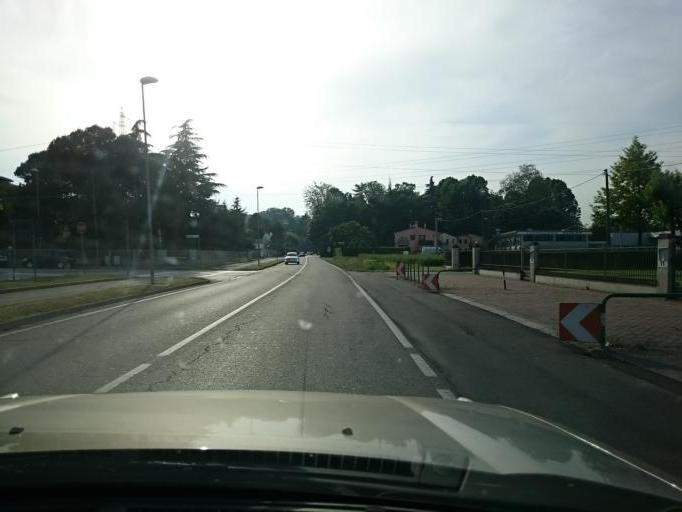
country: IT
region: Veneto
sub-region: Provincia di Padova
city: San Vito
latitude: 45.4139
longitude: 11.9714
